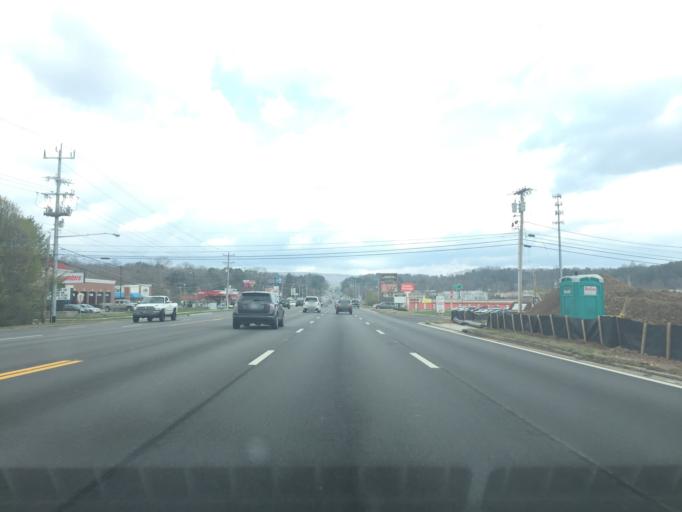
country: US
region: Tennessee
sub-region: Hamilton County
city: Falling Water
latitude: 35.1499
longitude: -85.2491
